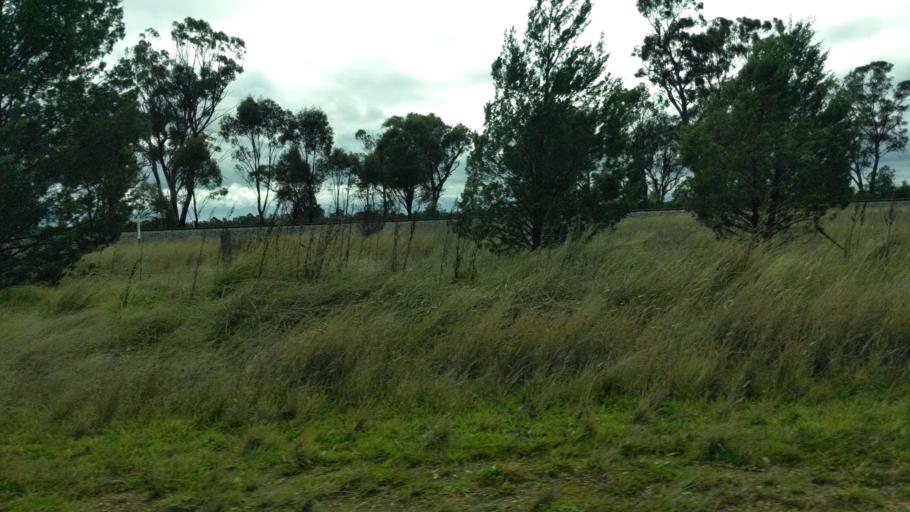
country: AU
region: New South Wales
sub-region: Narrandera
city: Narrandera
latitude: -34.7496
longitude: 146.8310
